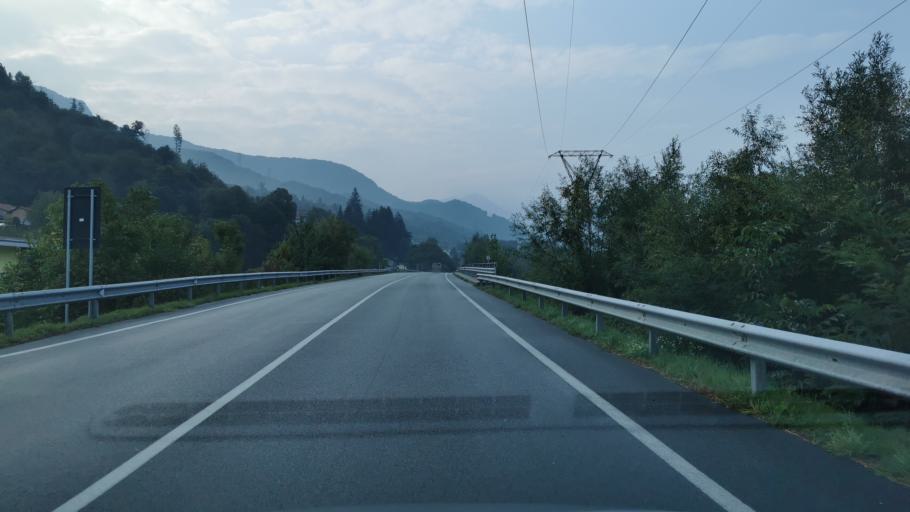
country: IT
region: Piedmont
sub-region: Provincia di Cuneo
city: Robilante
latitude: 44.2922
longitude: 7.5179
